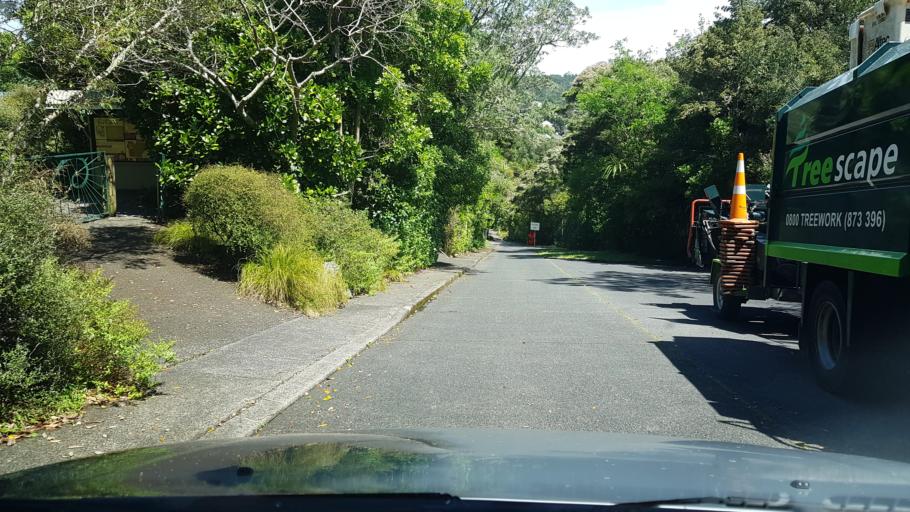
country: NZ
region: Auckland
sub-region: Auckland
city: North Shore
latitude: -36.8103
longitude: 174.7050
